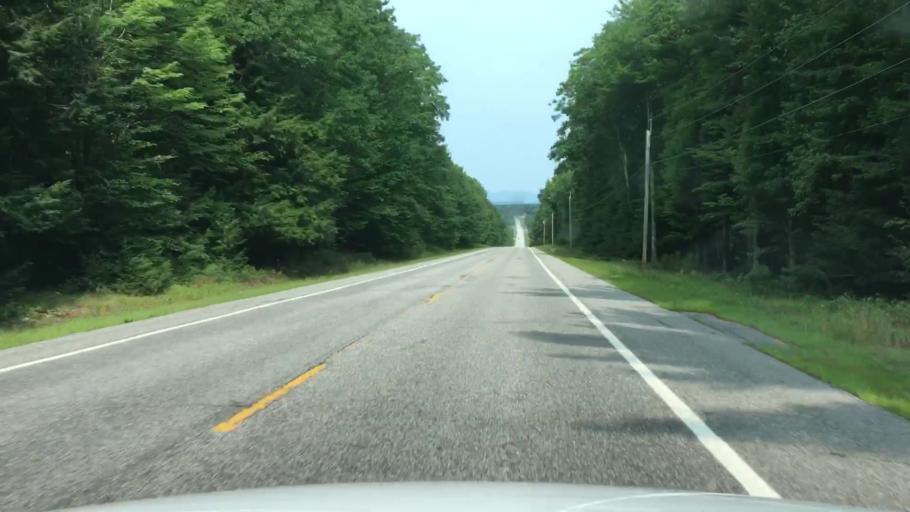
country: US
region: Maine
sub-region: Kennebec County
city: Wayne
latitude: 44.3790
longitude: -70.1013
